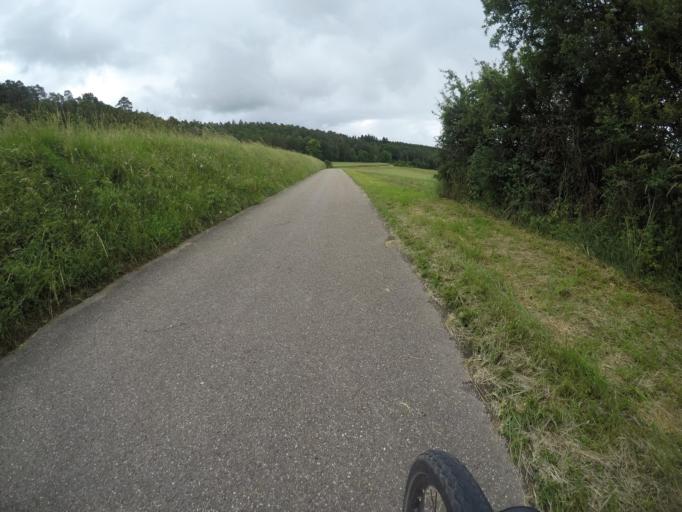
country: DE
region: Baden-Wuerttemberg
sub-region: Regierungsbezirk Stuttgart
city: Aidlingen
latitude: 48.6738
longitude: 8.8796
